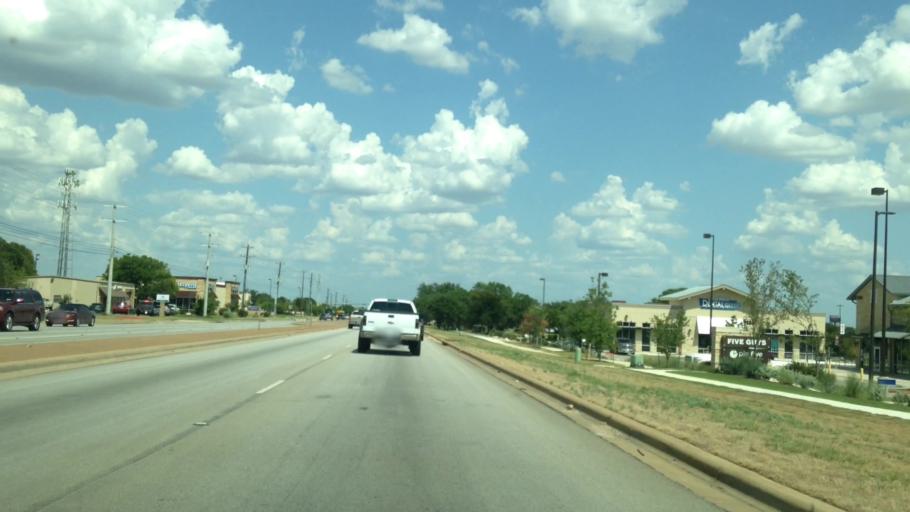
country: US
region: Texas
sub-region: Williamson County
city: Georgetown
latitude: 30.6329
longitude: -97.7000
